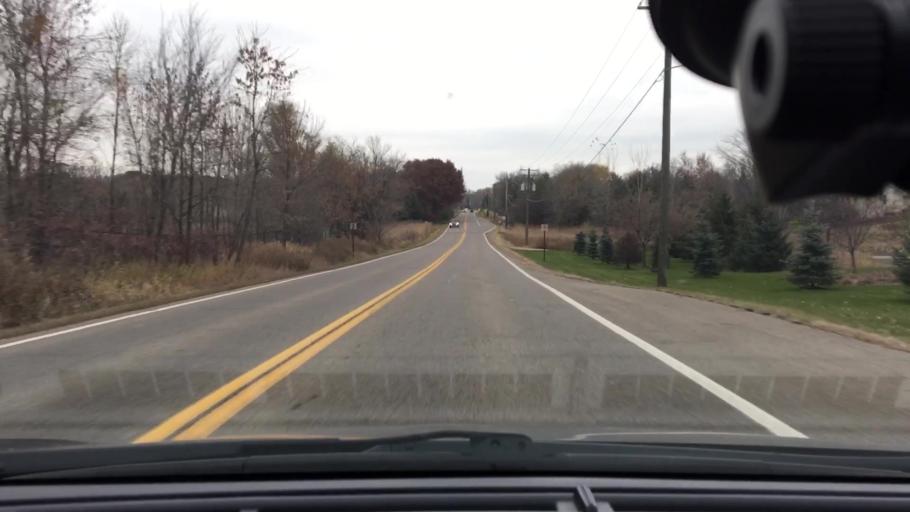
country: US
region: Minnesota
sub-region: Hennepin County
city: Corcoran
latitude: 45.1006
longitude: -93.5122
